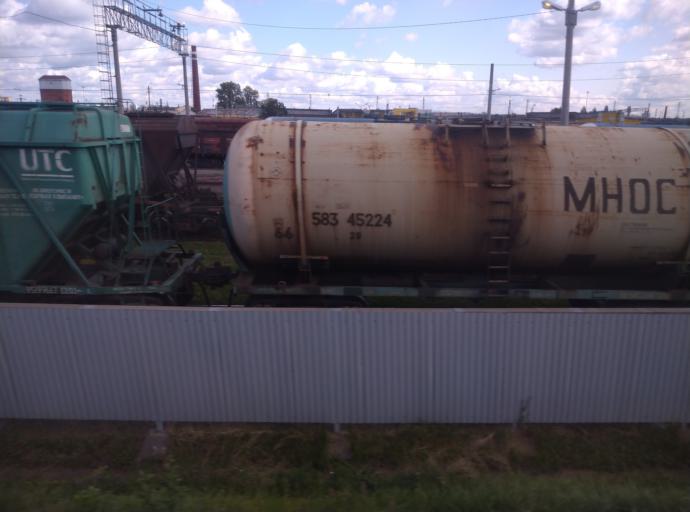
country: RU
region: St.-Petersburg
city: Obukhovo
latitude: 59.8704
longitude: 30.4194
